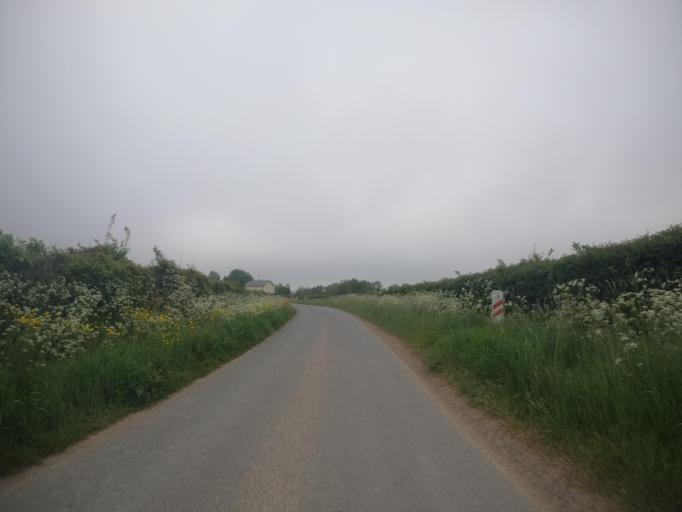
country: FR
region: Poitou-Charentes
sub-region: Departement des Deux-Sevres
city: Mauze-Thouarsais
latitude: 46.9005
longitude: -0.3320
